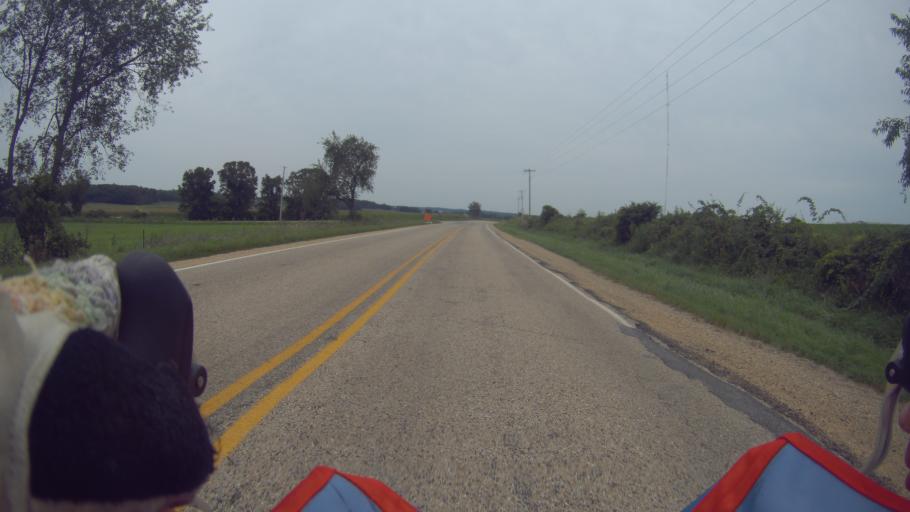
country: US
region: Wisconsin
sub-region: Dane County
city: Belleville
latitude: 42.9068
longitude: -89.5589
